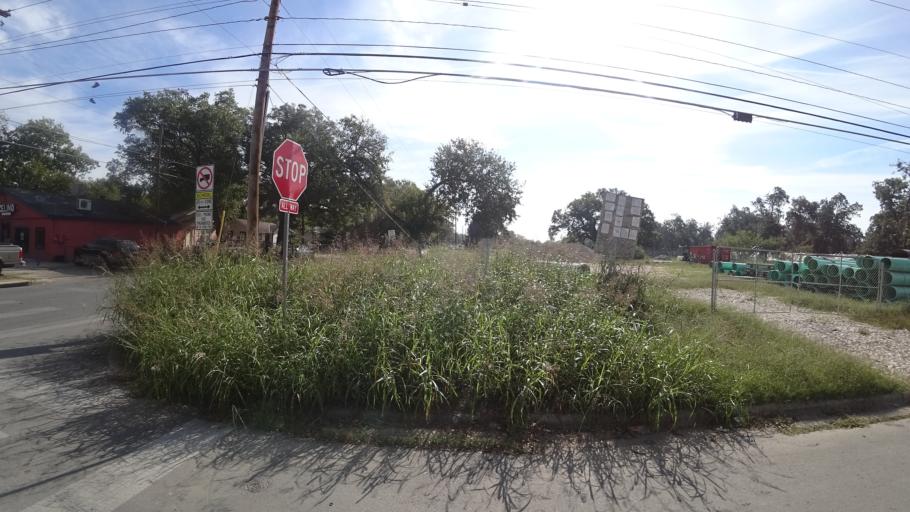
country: US
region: Texas
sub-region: Travis County
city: Austin
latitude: 30.2624
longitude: -97.7039
